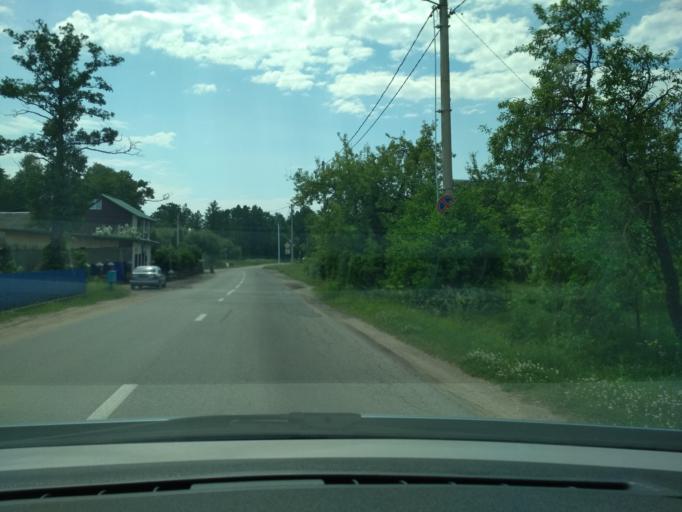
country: BY
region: Grodnenskaya
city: Astravyets
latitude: 54.6094
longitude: 25.9486
